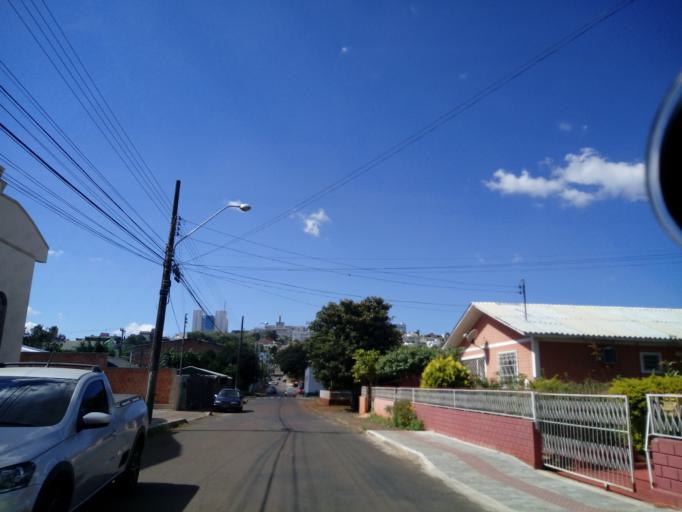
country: BR
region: Santa Catarina
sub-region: Chapeco
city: Chapeco
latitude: -27.1100
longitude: -52.6055
